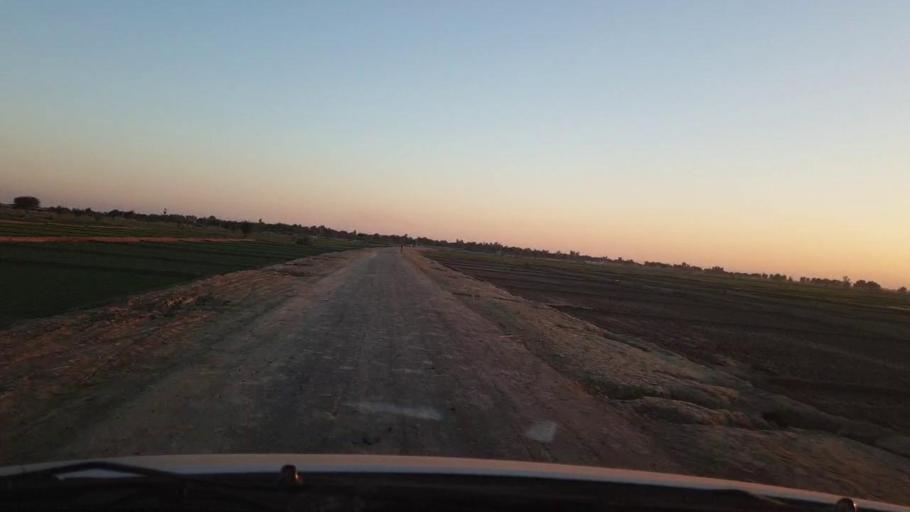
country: PK
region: Sindh
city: Johi
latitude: 26.8377
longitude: 67.4415
